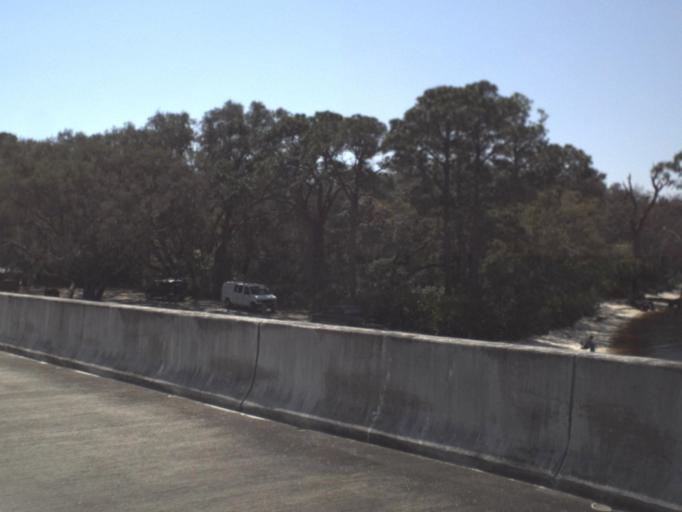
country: US
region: Florida
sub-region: Wakulla County
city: Crawfordville
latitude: 29.9614
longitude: -84.3846
